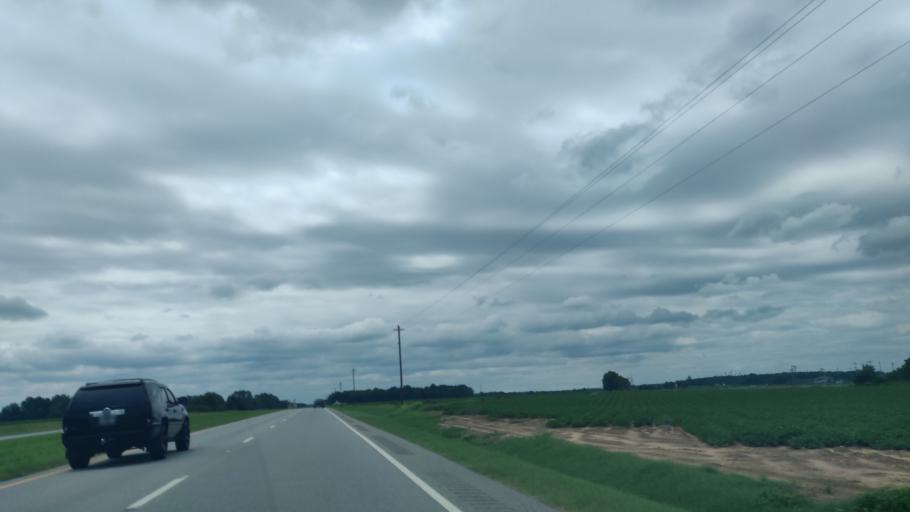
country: US
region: Georgia
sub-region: Terrell County
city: Dawson
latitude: 31.8272
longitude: -84.4627
